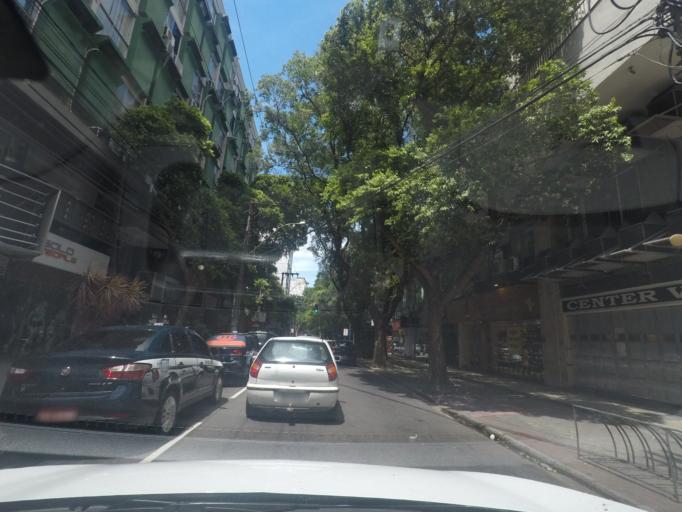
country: BR
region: Rio de Janeiro
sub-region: Niteroi
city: Niteroi
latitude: -22.9048
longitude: -43.1104
